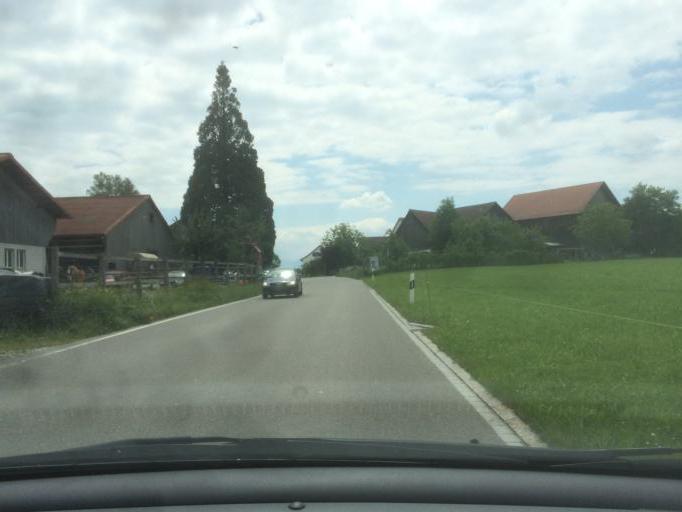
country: CH
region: Zurich
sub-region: Bezirk Hinwil
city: Wetzikon / Robenhausen
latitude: 47.3458
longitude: 8.7676
